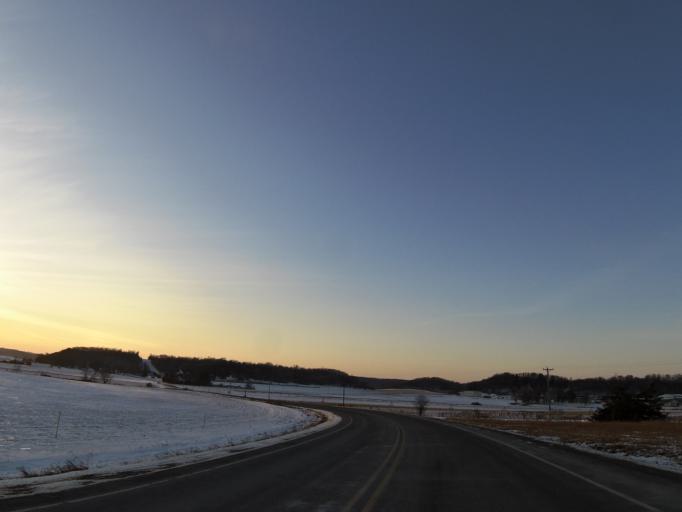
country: US
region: Wisconsin
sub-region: Pierce County
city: River Falls
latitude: 44.8767
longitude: -92.6507
